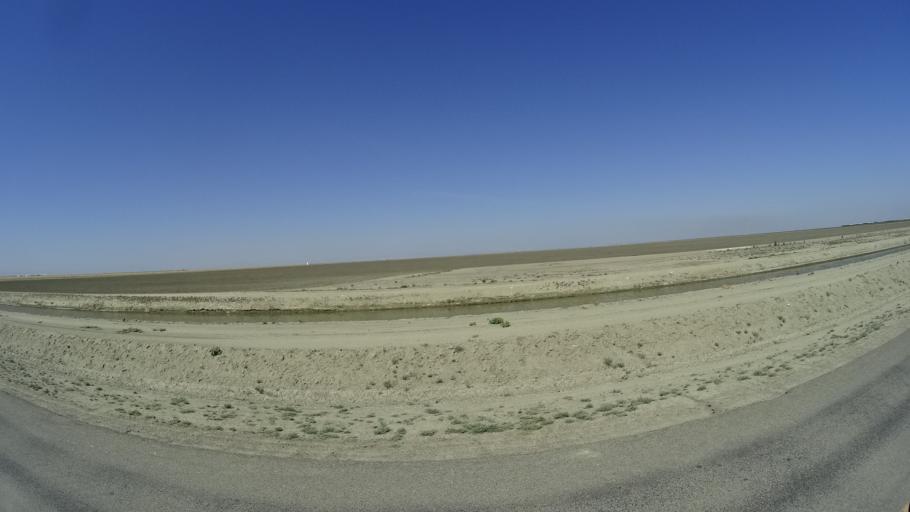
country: US
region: California
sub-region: Tulare County
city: Alpaugh
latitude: 35.9801
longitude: -119.5365
